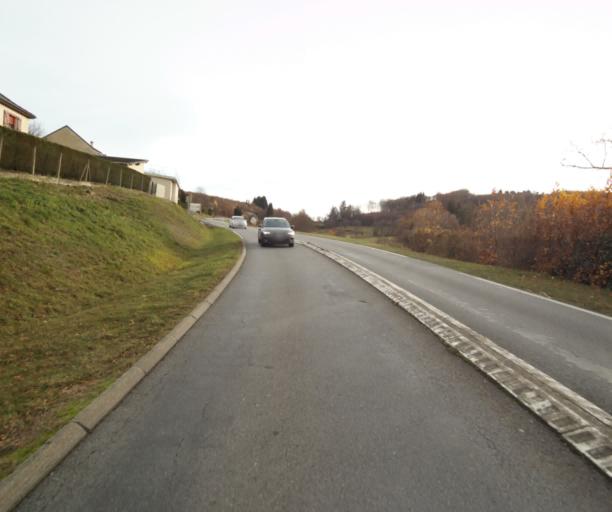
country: FR
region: Limousin
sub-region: Departement de la Correze
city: Sainte-Fortunade
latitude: 45.2022
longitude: 1.7709
